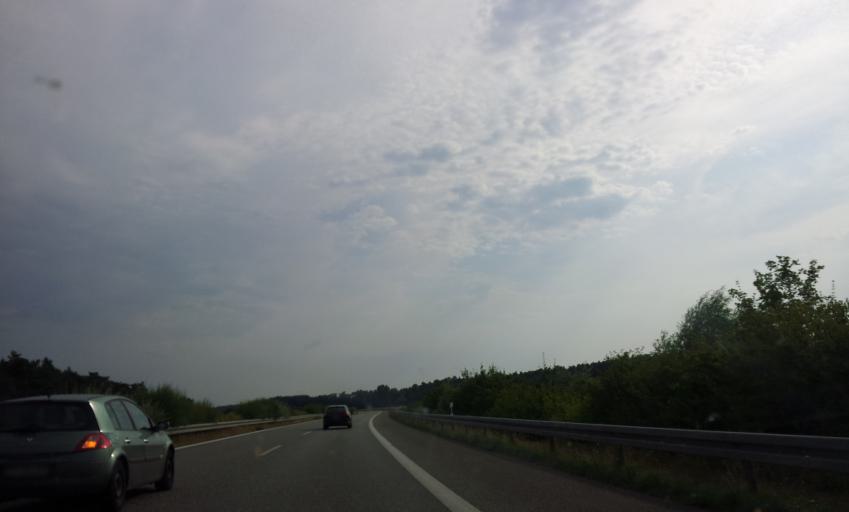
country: DE
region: Brandenburg
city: Ludwigsfelde
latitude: 52.2792
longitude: 13.2761
